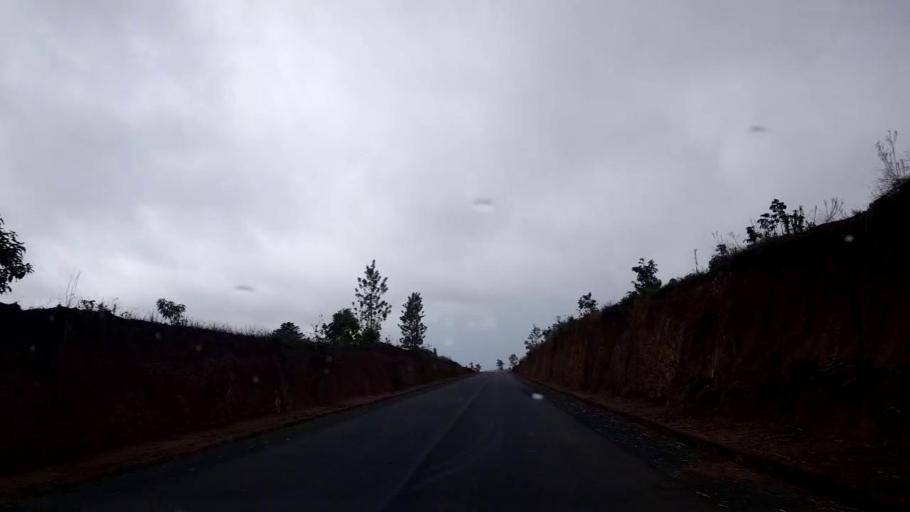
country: RW
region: Northern Province
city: Byumba
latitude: -1.4273
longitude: 30.2657
